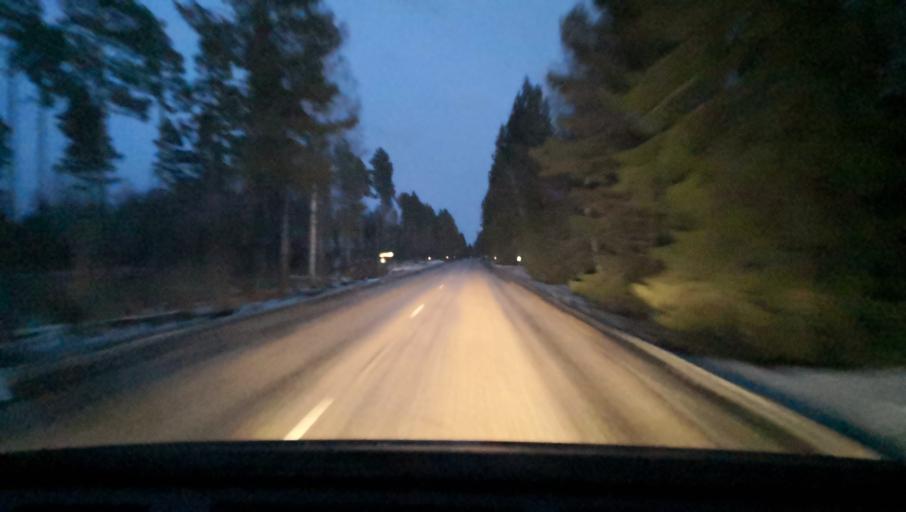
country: SE
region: Vaestmanland
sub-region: Sala Kommun
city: Sala
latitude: 59.8392
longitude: 16.4977
